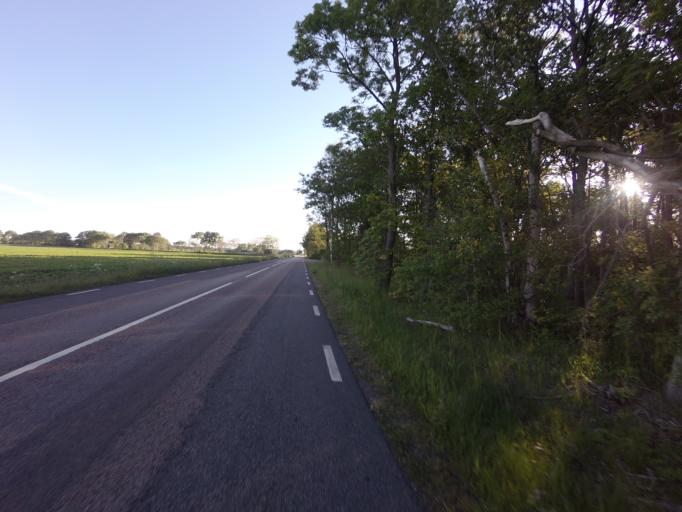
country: SE
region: Skane
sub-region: Hoganas Kommun
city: Hoganas
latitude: 56.2067
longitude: 12.6752
